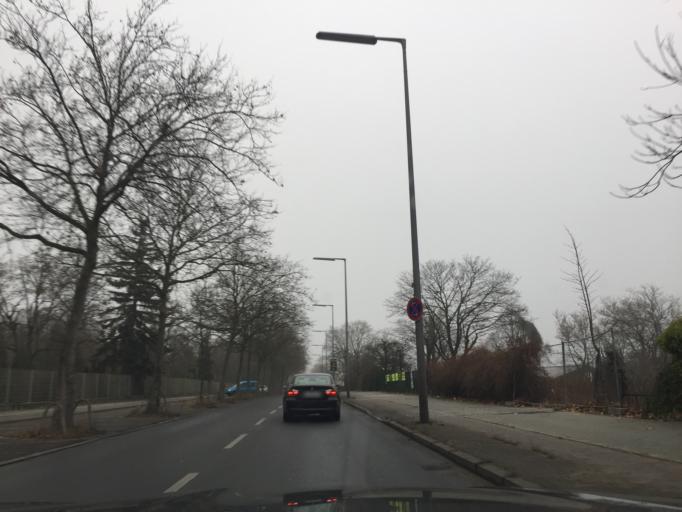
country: DE
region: Berlin
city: Westend
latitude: 52.5221
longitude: 13.2797
